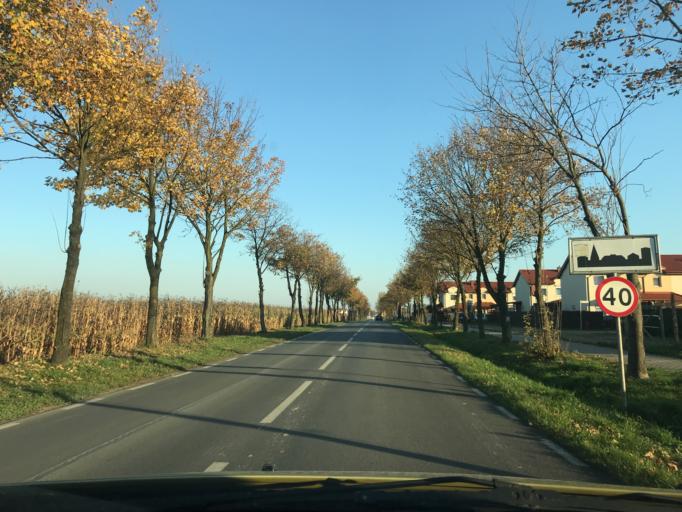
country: PL
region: Greater Poland Voivodeship
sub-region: Powiat poznanski
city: Baranowo
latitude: 52.3926
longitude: 16.7714
